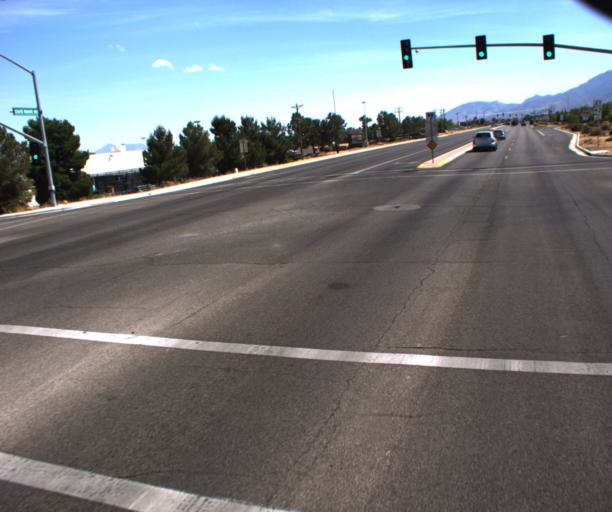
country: US
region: Arizona
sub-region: Cochise County
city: Sierra Vista
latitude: 31.5621
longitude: -110.2574
